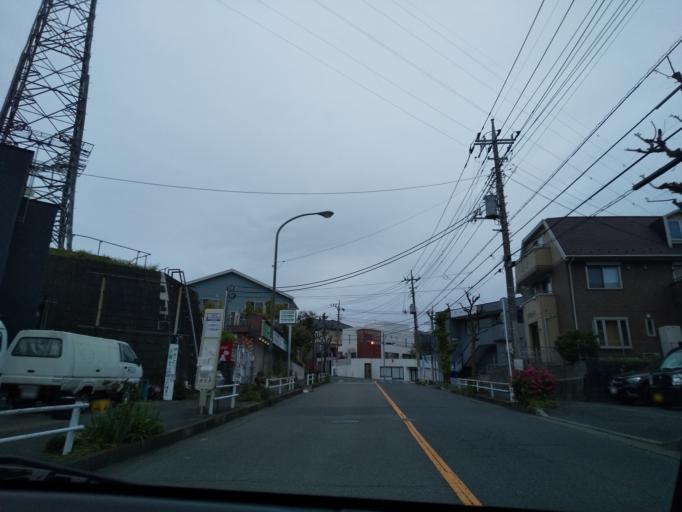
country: JP
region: Tokyo
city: Hino
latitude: 35.6332
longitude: 139.3747
